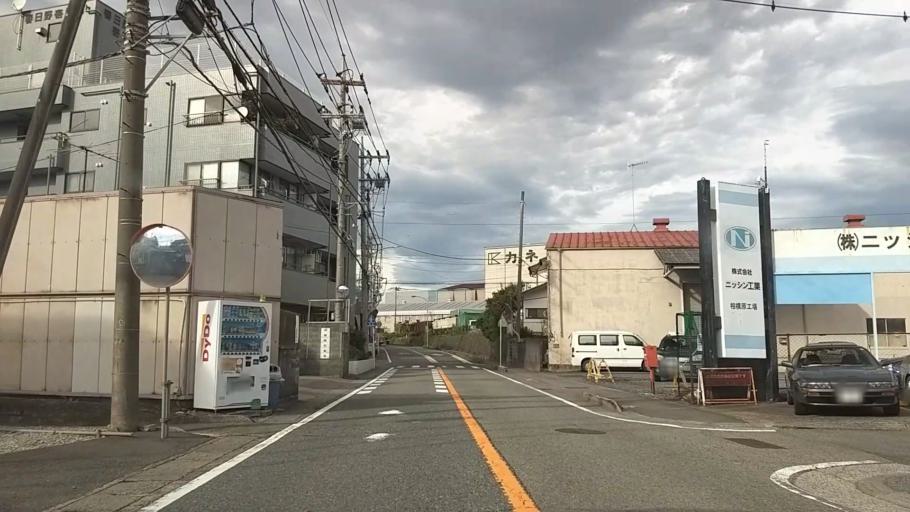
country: JP
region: Kanagawa
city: Zama
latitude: 35.5573
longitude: 139.3383
